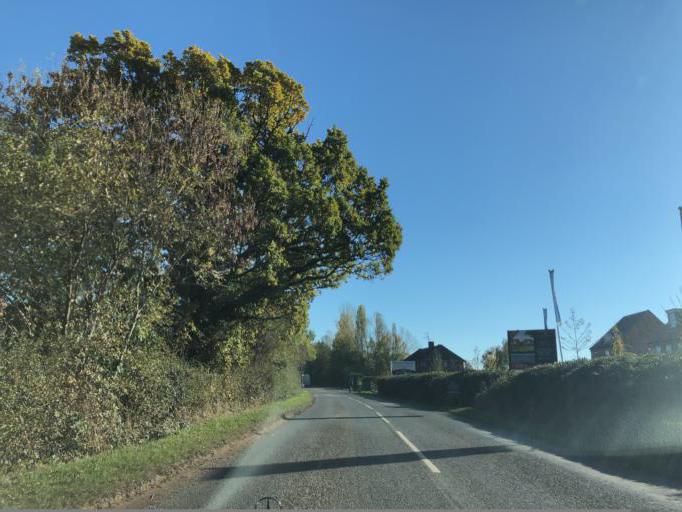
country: GB
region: England
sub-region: Warwickshire
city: Royal Leamington Spa
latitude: 52.2649
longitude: -1.5486
